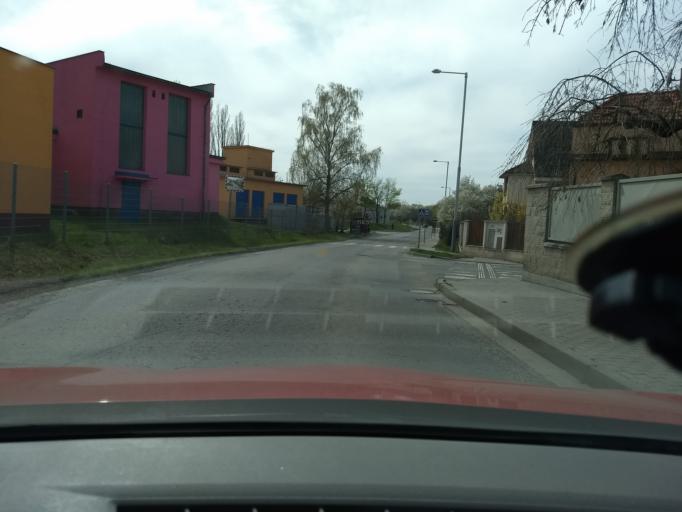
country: CZ
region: Central Bohemia
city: Hostivice
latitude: 50.0663
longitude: 14.2892
